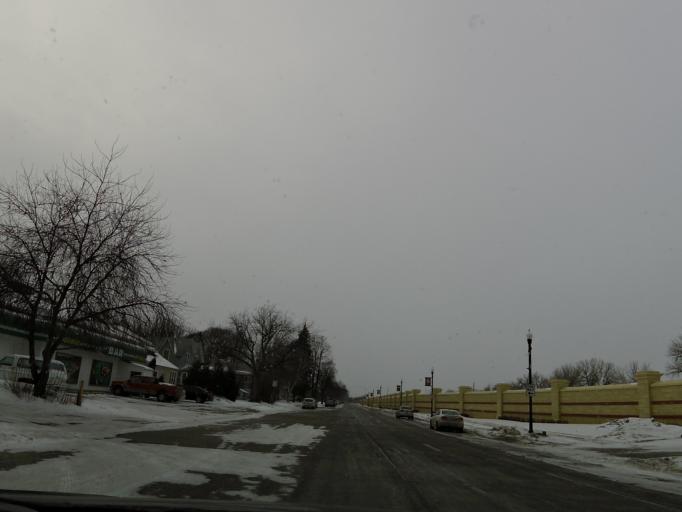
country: US
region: North Dakota
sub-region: Grand Forks County
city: Grand Forks
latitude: 47.9273
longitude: -97.0343
